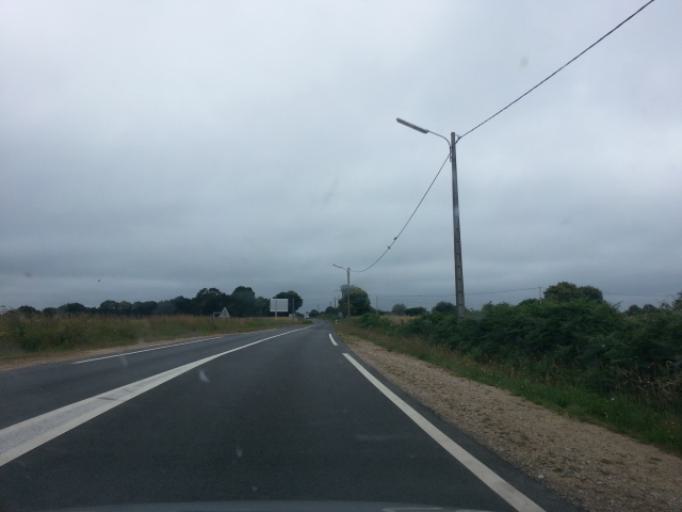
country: FR
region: Brittany
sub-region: Departement du Morbihan
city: Plouray
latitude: 48.1414
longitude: -3.3940
